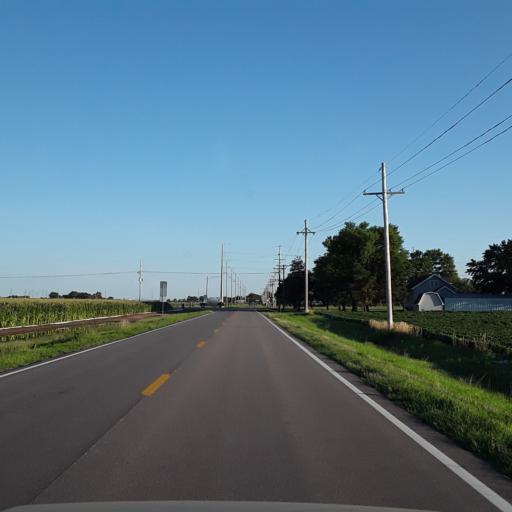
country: US
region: Nebraska
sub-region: Hall County
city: Grand Island
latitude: 40.9472
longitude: -98.3206
